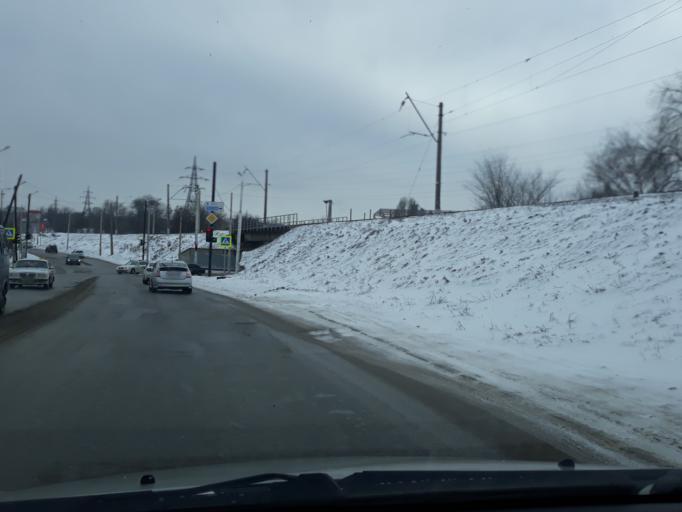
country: RU
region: Rostov
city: Taganrog
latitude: 47.2528
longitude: 38.8963
